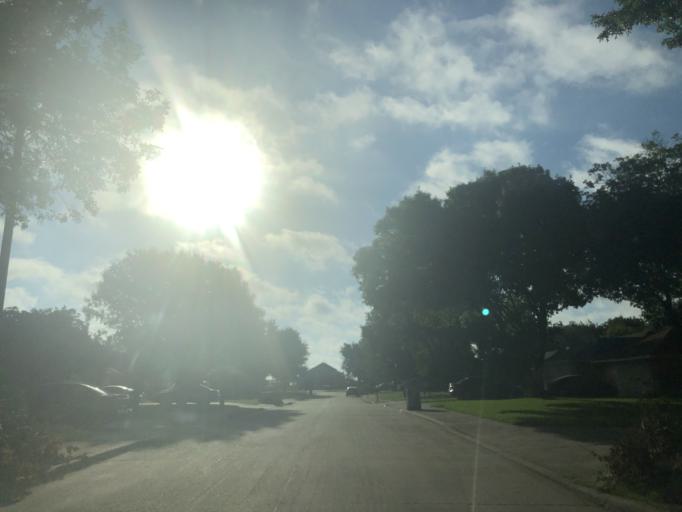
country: US
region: Texas
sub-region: Dallas County
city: Duncanville
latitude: 32.6710
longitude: -96.9113
